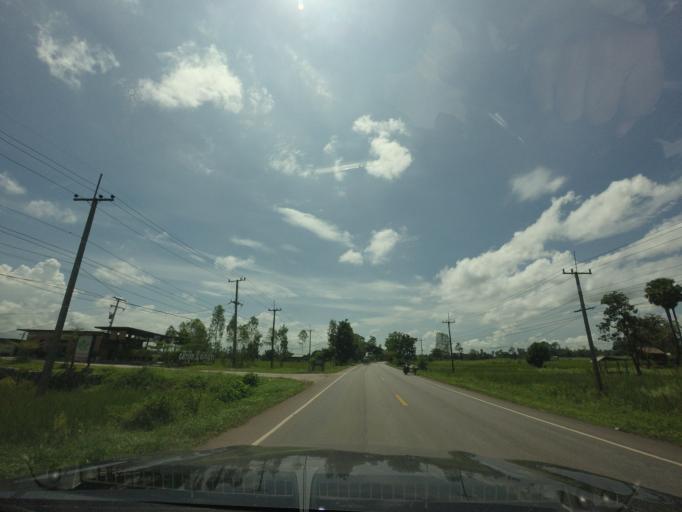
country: TH
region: Nong Khai
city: Pho Tak
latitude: 17.7647
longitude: 102.3973
